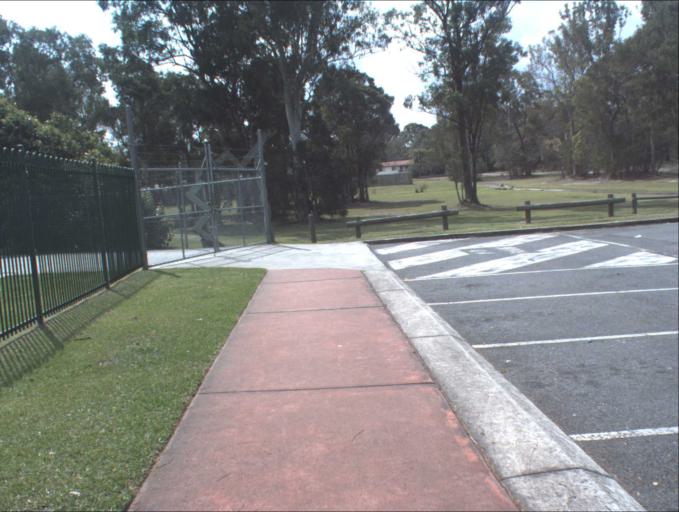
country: AU
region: Queensland
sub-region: Logan
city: Waterford West
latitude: -27.6717
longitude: 153.1284
